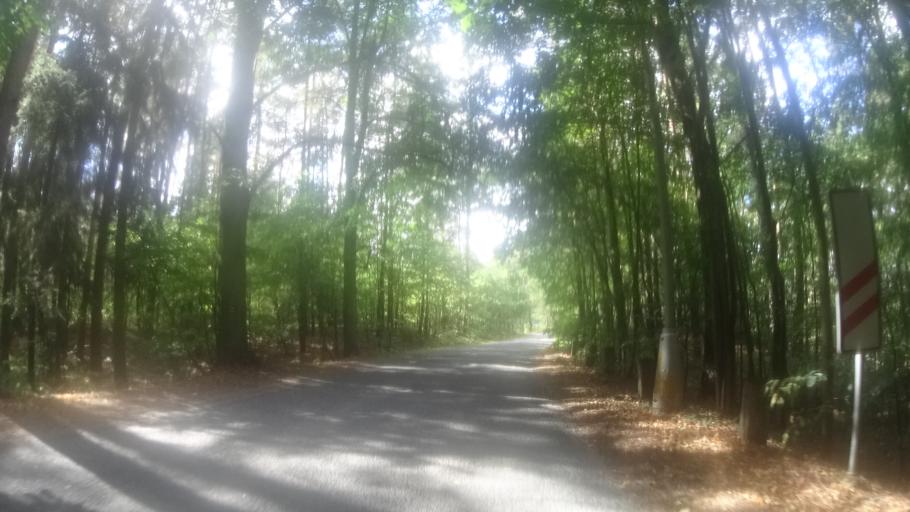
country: CZ
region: Pardubicky
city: Horni Jeleni
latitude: 50.0633
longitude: 16.1401
